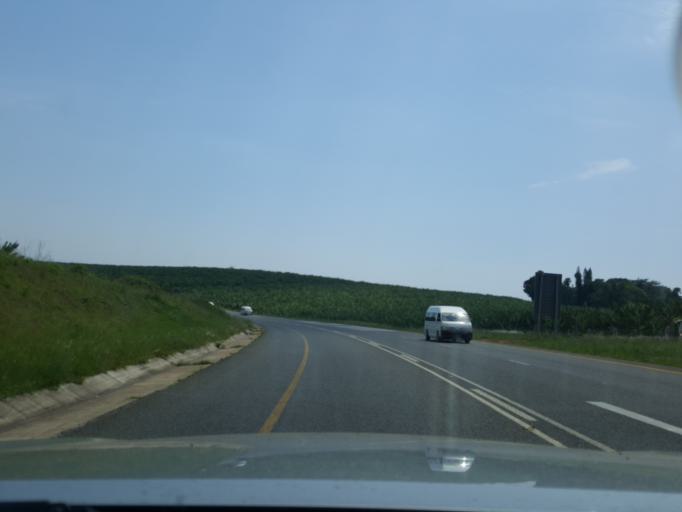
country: ZA
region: Mpumalanga
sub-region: Ehlanzeni District
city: White River
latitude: -25.0799
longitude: 31.1020
